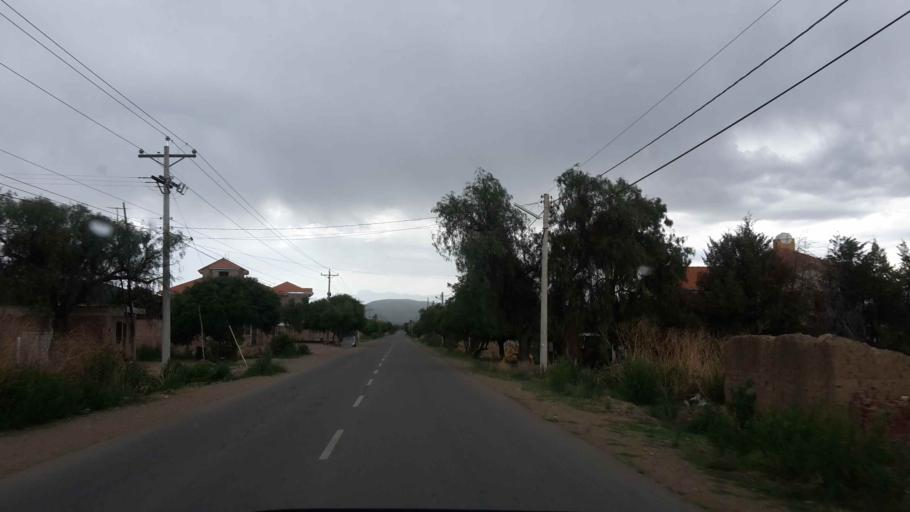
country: BO
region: Cochabamba
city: Tarata
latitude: -17.5895
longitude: -66.0470
